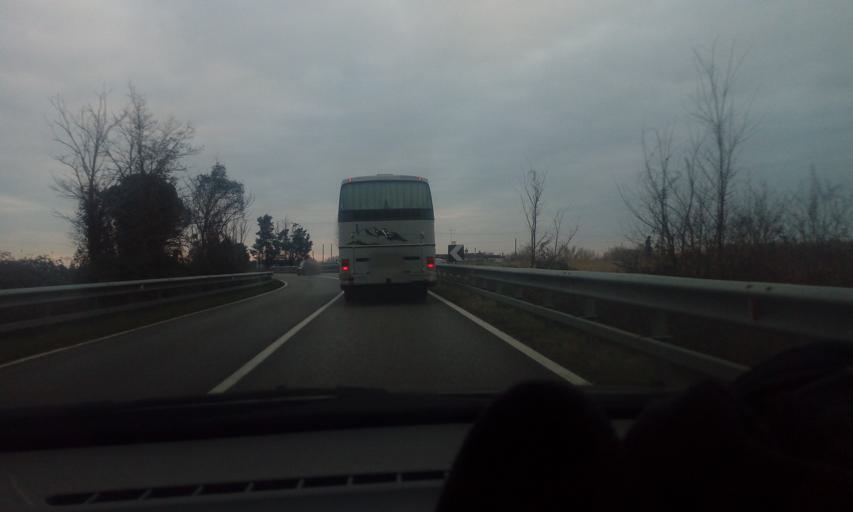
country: IT
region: Friuli Venezia Giulia
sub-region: Provincia di Udine
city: Aquileia
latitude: 45.7262
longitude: 13.3865
